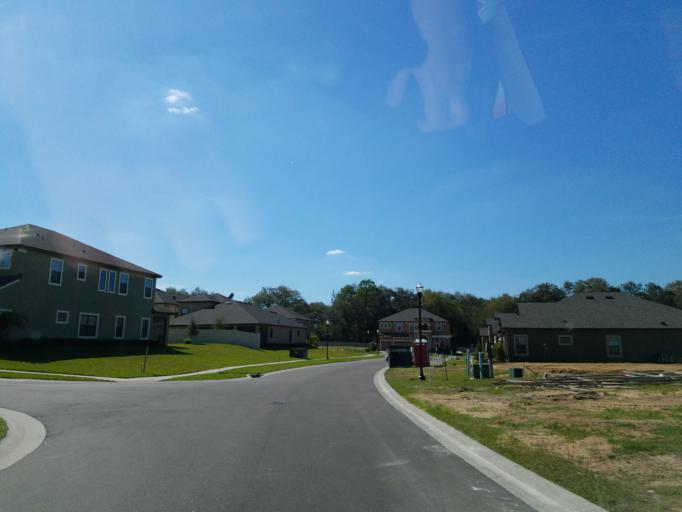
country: US
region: Florida
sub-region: Hillsborough County
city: Brandon
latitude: 27.9284
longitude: -82.2678
